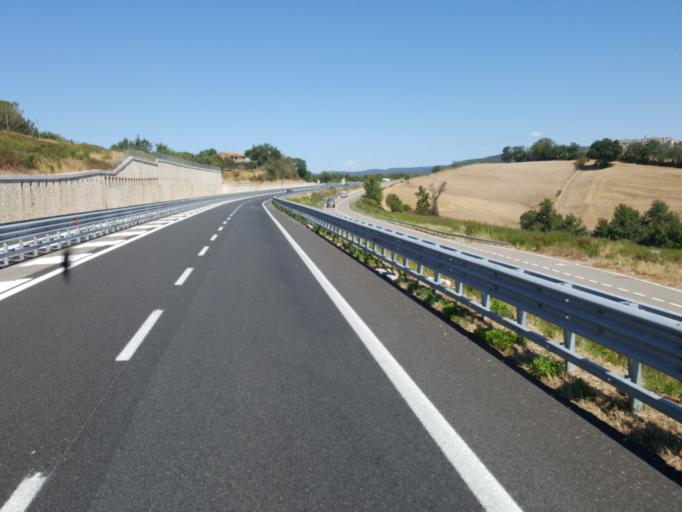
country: IT
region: Tuscany
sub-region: Provincia di Grosseto
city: Civitella Marittima
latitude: 42.9673
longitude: 11.2812
